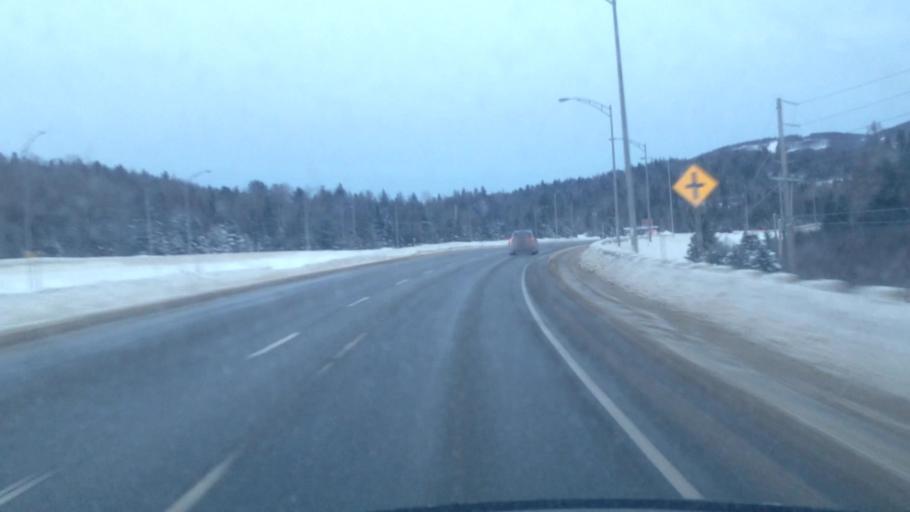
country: CA
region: Quebec
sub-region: Laurentides
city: Mont-Tremblant
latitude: 46.1128
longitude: -74.5210
